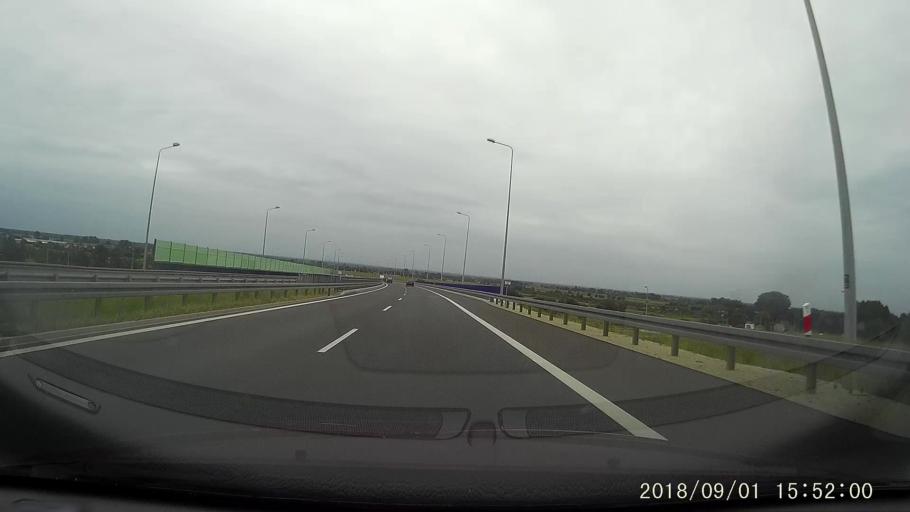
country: PL
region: Lubusz
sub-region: Powiat gorzowski
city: Jenin
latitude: 52.7156
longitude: 15.1578
